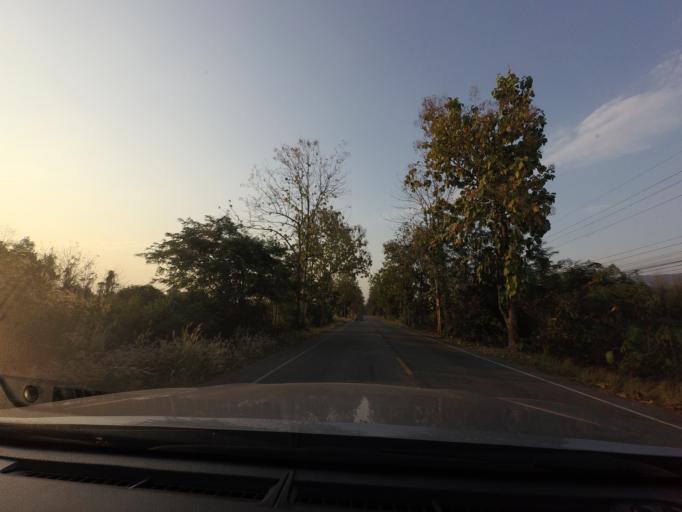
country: TH
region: Phitsanulok
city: Wang Thong
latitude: 16.6927
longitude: 100.5228
